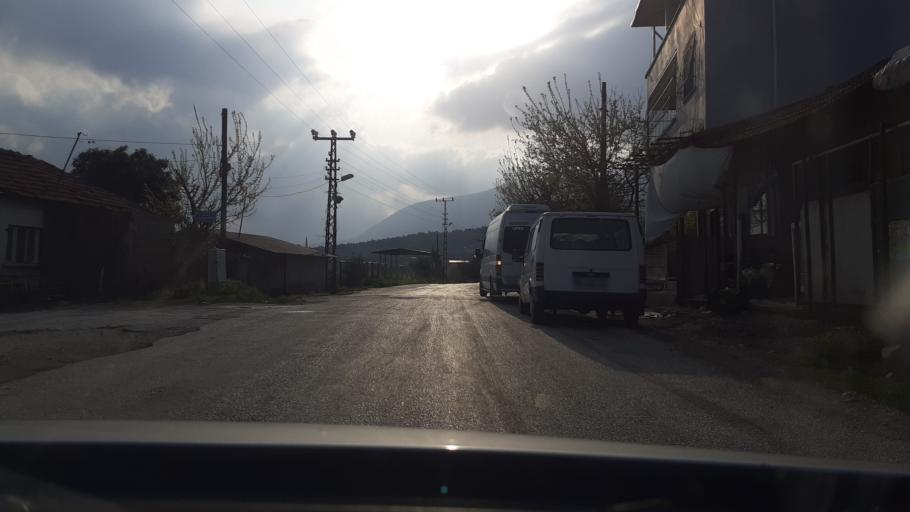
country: TR
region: Hatay
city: Kirikhan
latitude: 36.4999
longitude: 36.3357
